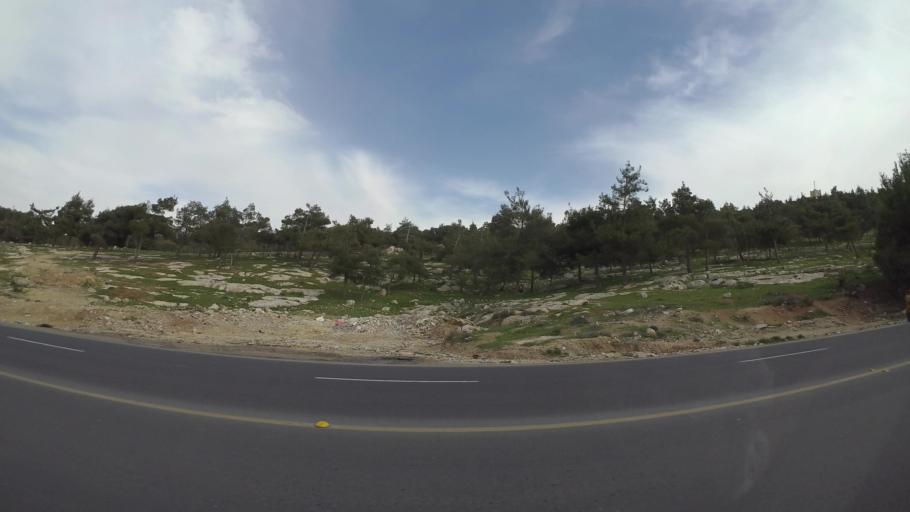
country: JO
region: Amman
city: Amman
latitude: 32.0155
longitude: 35.9352
